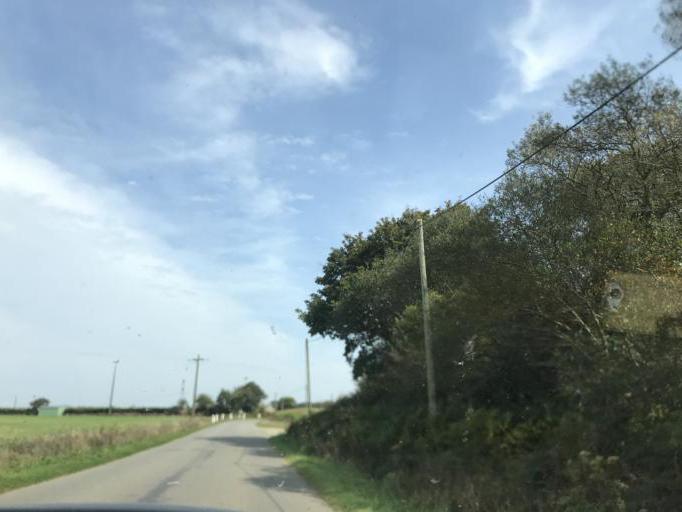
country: FR
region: Brittany
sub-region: Departement du Finistere
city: Hanvec
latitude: 48.2889
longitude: -4.1110
